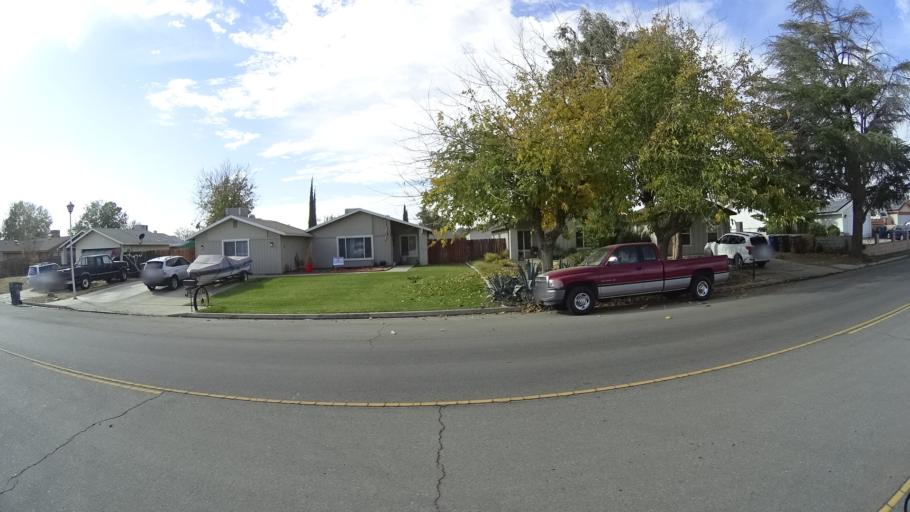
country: US
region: California
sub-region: Kern County
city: Greenacres
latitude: 35.3954
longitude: -119.1189
